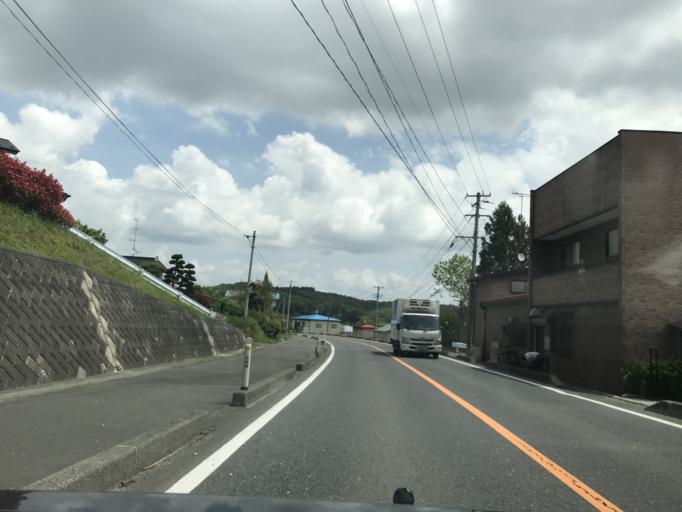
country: JP
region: Miyagi
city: Kogota
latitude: 38.6614
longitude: 141.0648
